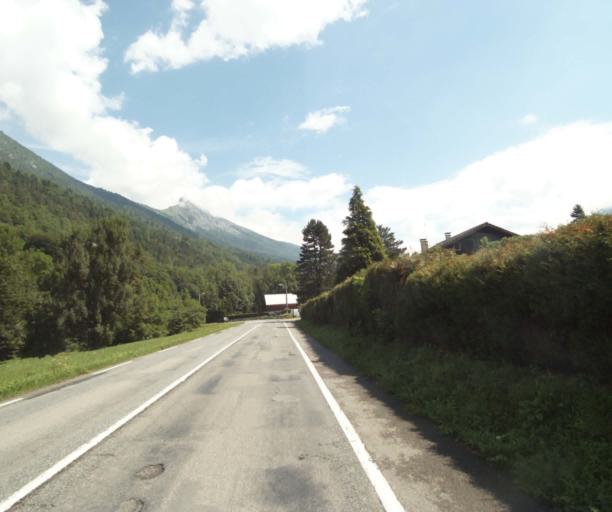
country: FR
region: Rhone-Alpes
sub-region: Departement de la Haute-Savoie
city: Thones
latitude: 45.8898
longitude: 6.3324
